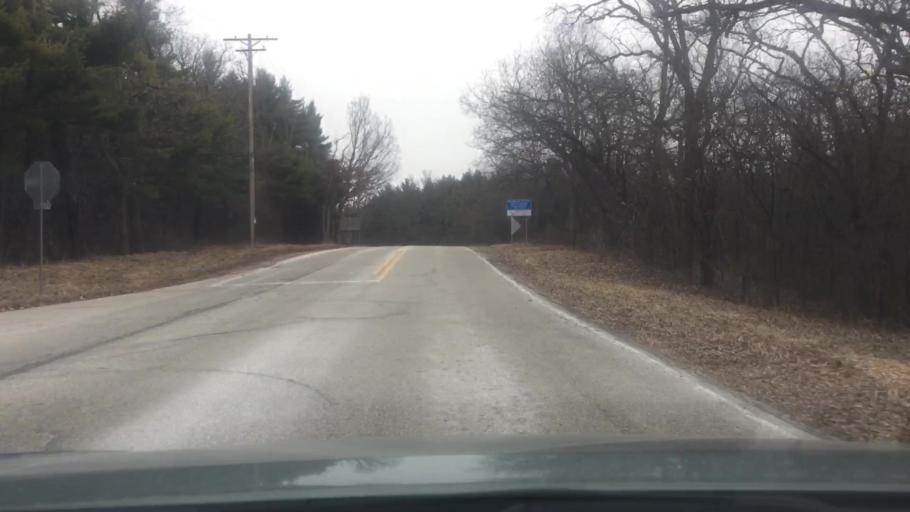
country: US
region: Wisconsin
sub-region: Waukesha County
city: North Prairie
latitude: 42.9422
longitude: -88.4397
